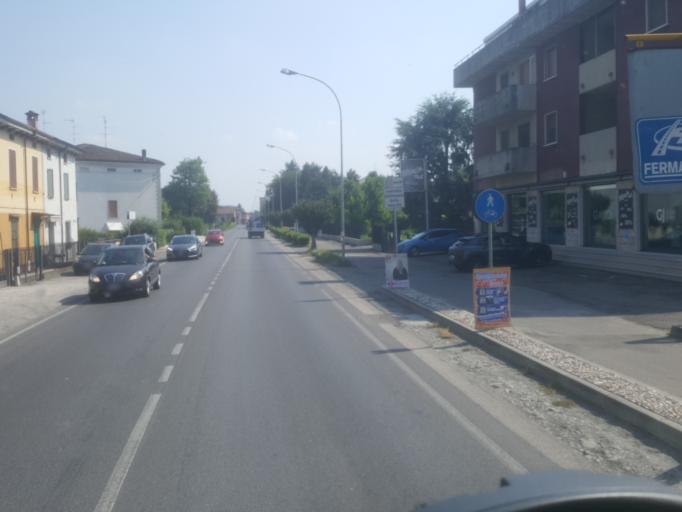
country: IT
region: Lombardy
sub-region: Provincia di Cremona
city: Casalmaggiore
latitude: 44.9935
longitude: 10.4181
